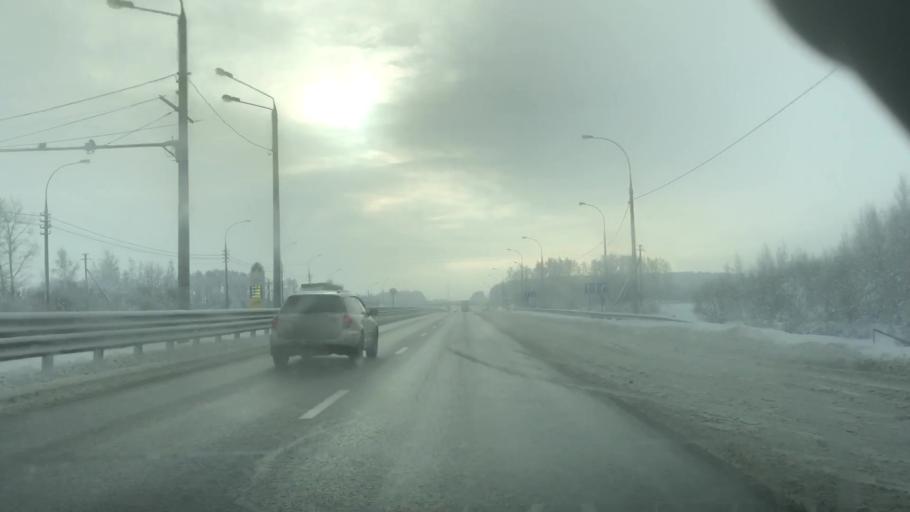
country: RU
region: Tula
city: Venev
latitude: 54.3406
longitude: 38.1545
